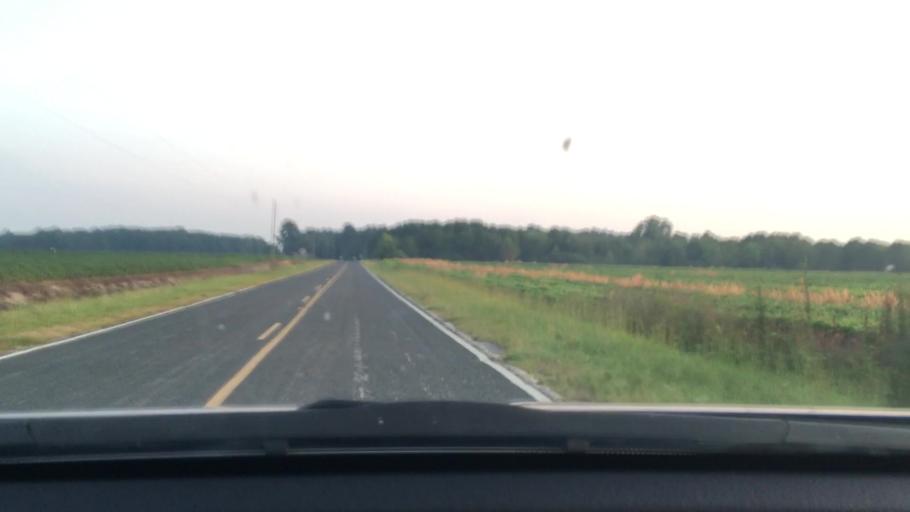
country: US
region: South Carolina
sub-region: Lee County
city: Bishopville
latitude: 34.2639
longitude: -80.1360
